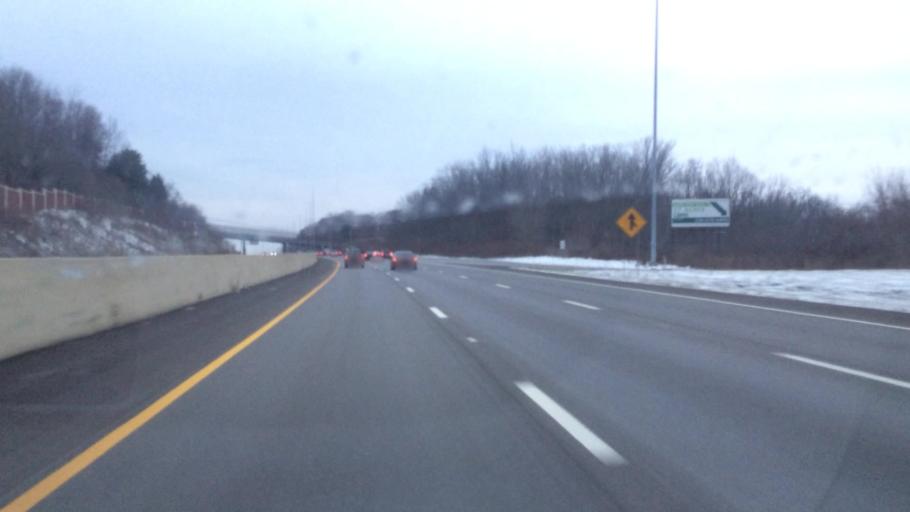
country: US
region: Ohio
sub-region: Summit County
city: Fairlawn
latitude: 41.1111
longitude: -81.6081
